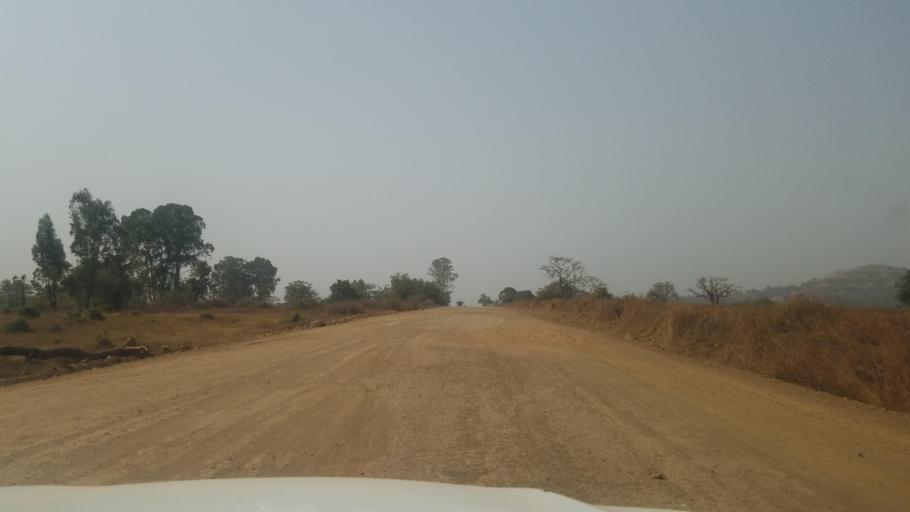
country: ET
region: Amhara
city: Bure
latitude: 10.9333
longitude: 36.4683
